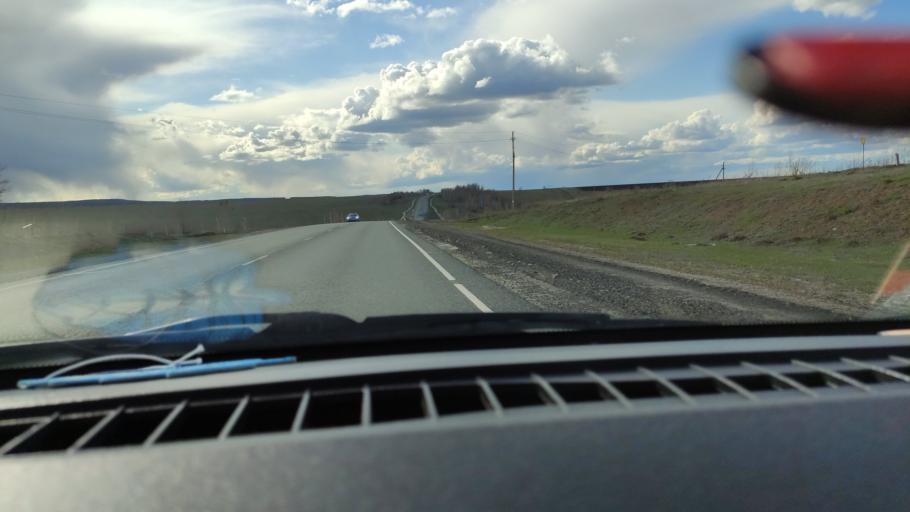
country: RU
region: Saratov
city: Shikhany
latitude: 52.1181
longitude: 47.2746
